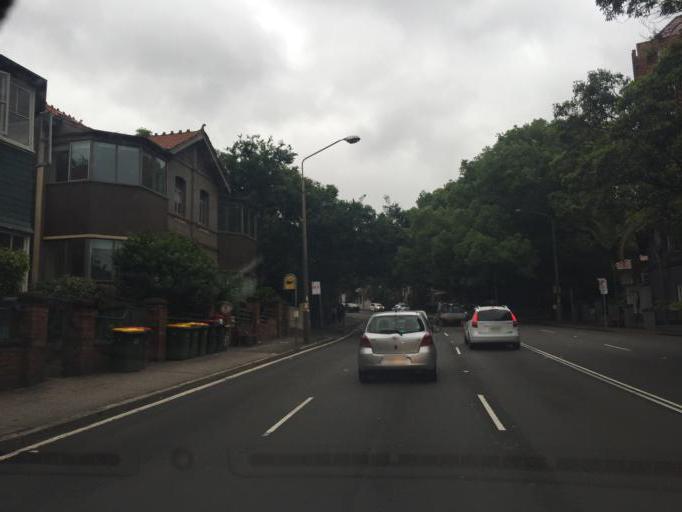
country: AU
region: New South Wales
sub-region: Woollahra
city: Darling Point
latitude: -33.8786
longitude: 151.2405
